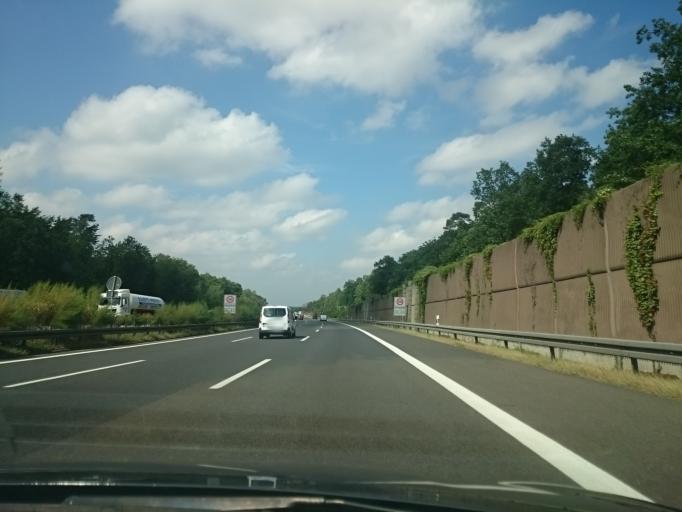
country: DE
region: Brandenburg
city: Woltersdorf
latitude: 52.4632
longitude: 13.7916
